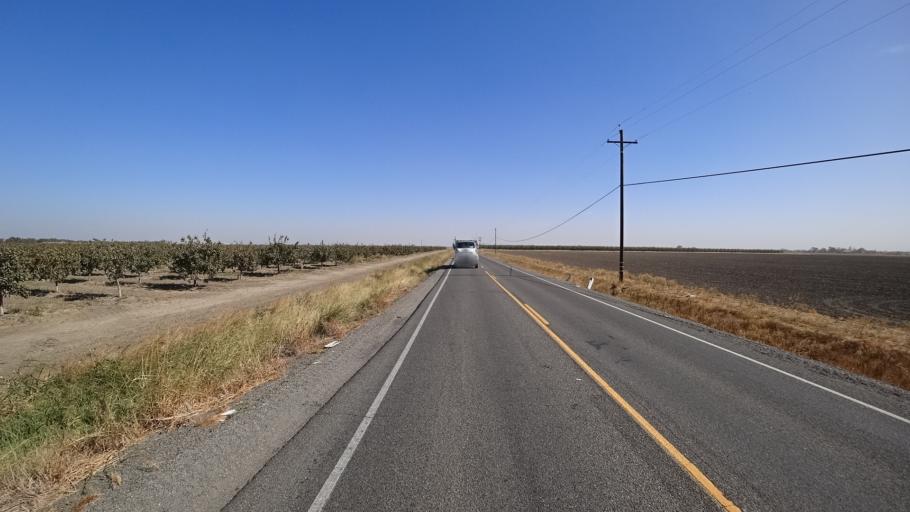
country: US
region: California
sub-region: Yolo County
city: Davis
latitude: 38.5906
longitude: -121.7623
